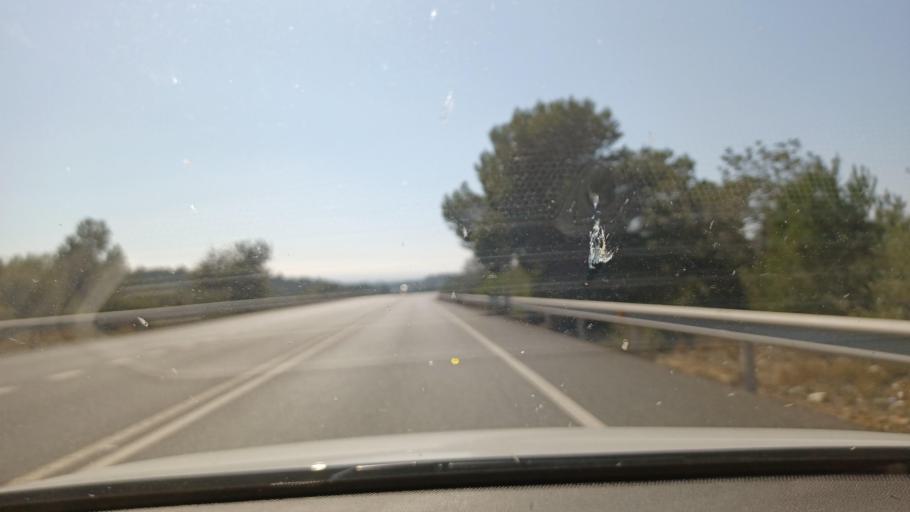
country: ES
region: Catalonia
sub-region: Provincia de Tarragona
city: El Perello
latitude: 40.8567
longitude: 0.7148
